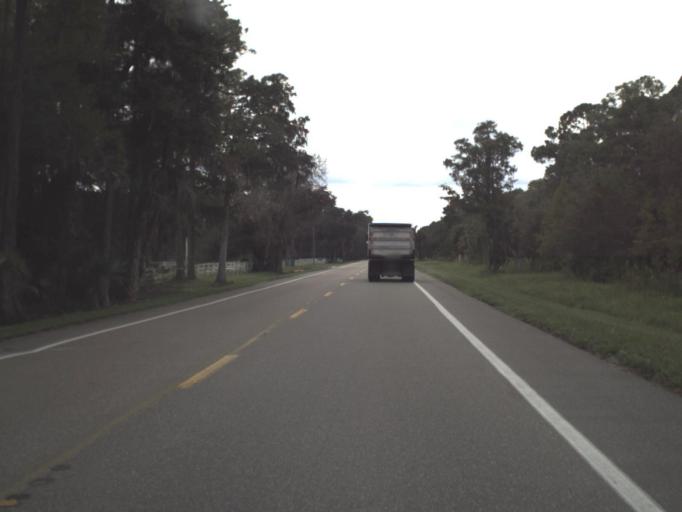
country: US
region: Florida
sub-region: Charlotte County
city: Cleveland
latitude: 26.9705
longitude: -81.7607
